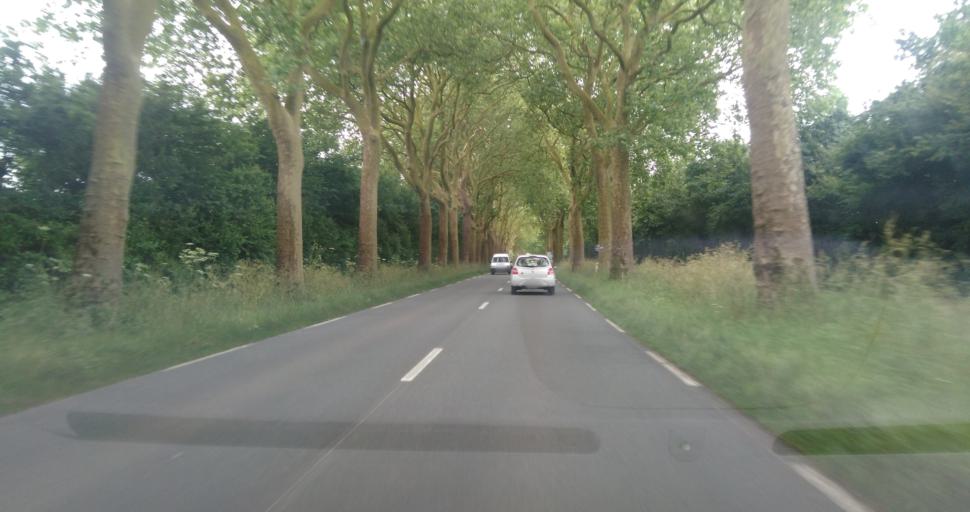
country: FR
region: Pays de la Loire
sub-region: Departement de la Vendee
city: Sainte-Hermine
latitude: 46.5613
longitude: -1.0723
